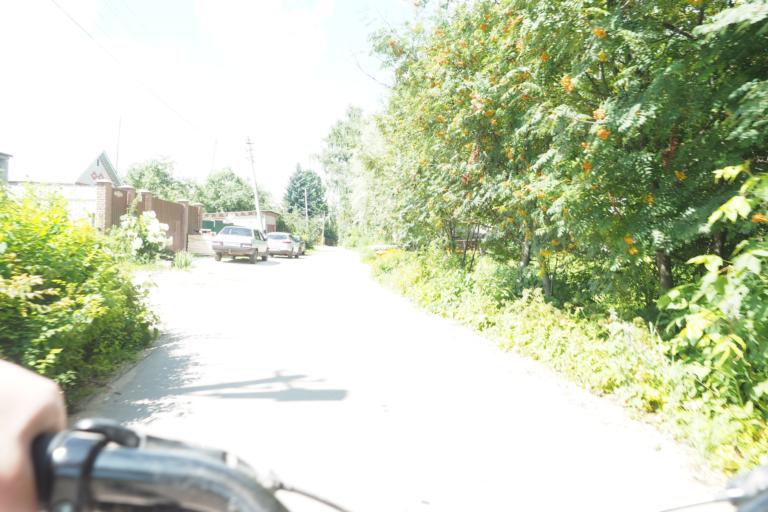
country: RU
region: Moskovskaya
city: Ramenskoye
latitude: 55.5794
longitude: 38.2649
